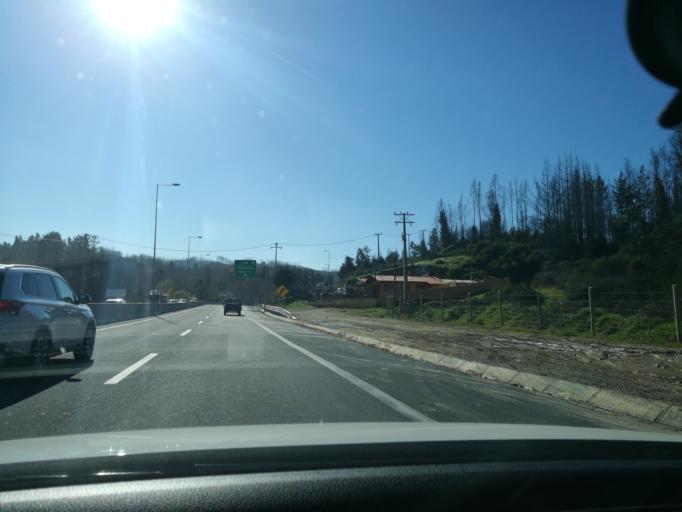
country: CL
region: Biobio
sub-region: Provincia de Concepcion
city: Chiguayante
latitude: -36.8570
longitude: -72.8813
